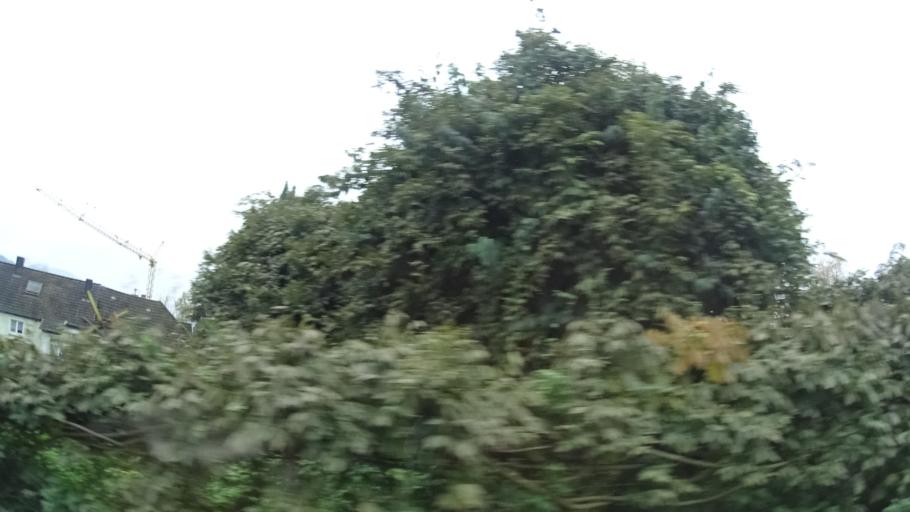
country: DE
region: Baden-Wuerttemberg
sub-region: Karlsruhe Region
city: Sinzheim
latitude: 48.7472
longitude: 8.1793
